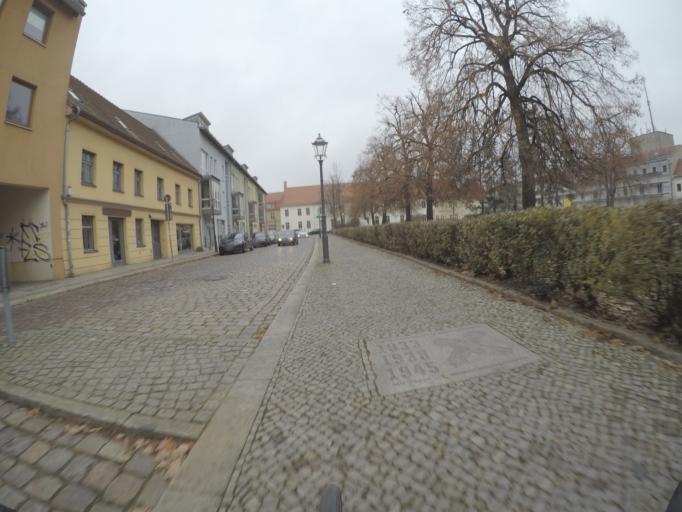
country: DE
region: Berlin
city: Kopenick Bezirk
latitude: 52.4467
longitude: 13.5782
